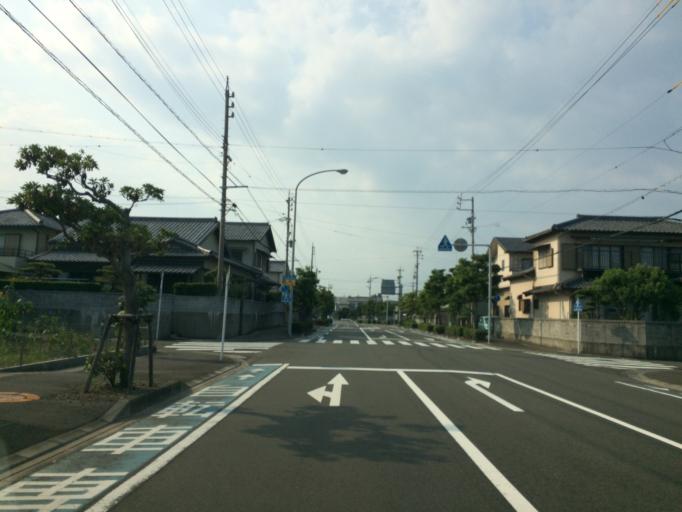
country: JP
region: Shizuoka
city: Shizuoka-shi
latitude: 34.9481
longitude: 138.4260
